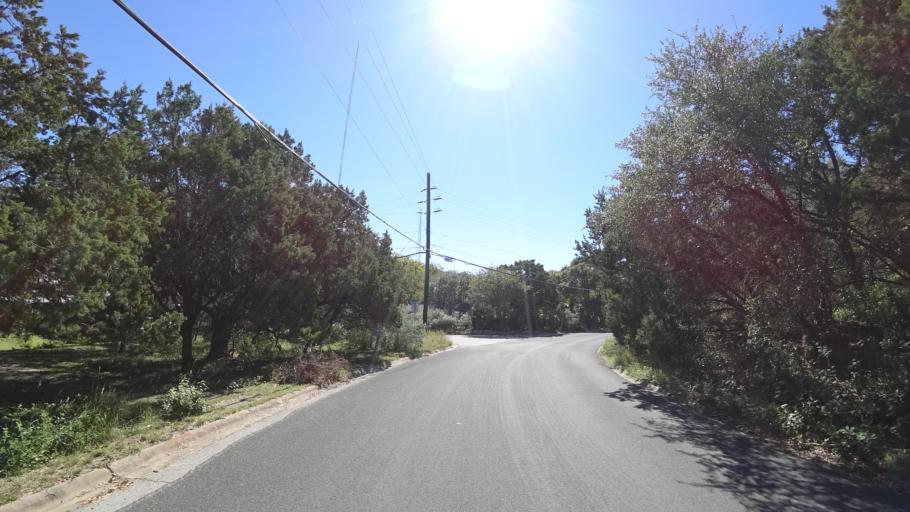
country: US
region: Texas
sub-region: Travis County
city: West Lake Hills
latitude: 30.3130
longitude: -97.7965
